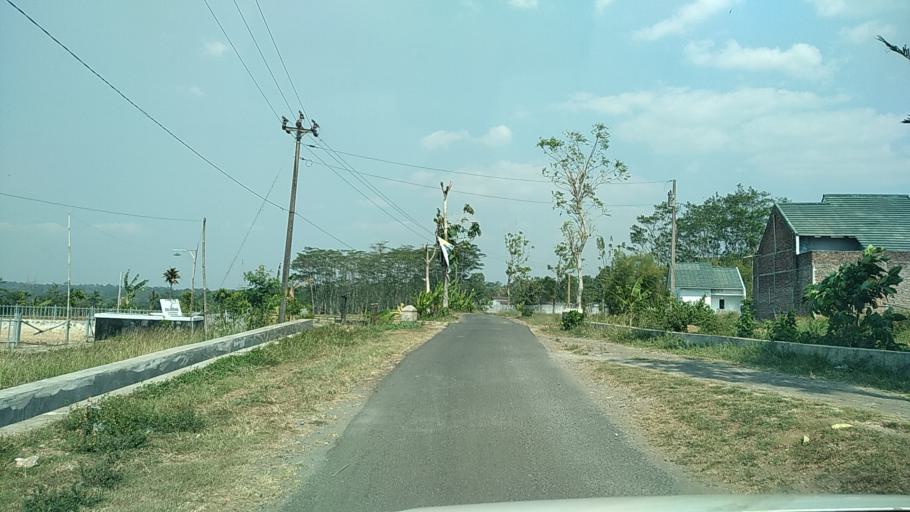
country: ID
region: Central Java
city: Ungaran
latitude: -7.0841
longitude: 110.3353
